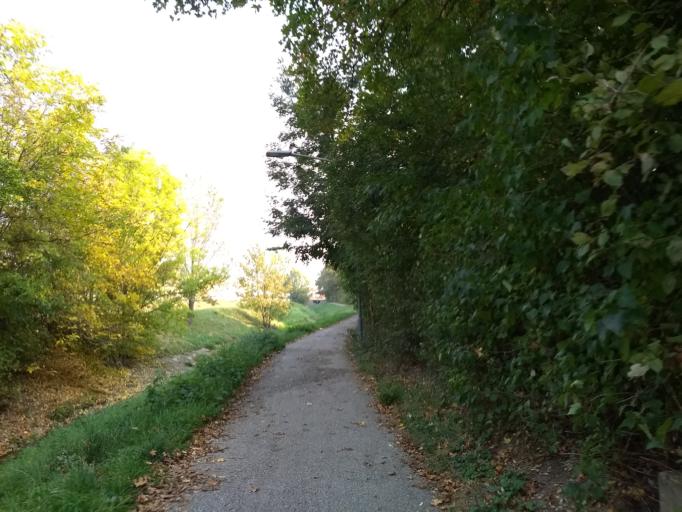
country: AT
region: Lower Austria
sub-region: Politischer Bezirk Modling
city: Brunn am Gebirge
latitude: 48.1270
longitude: 16.2955
